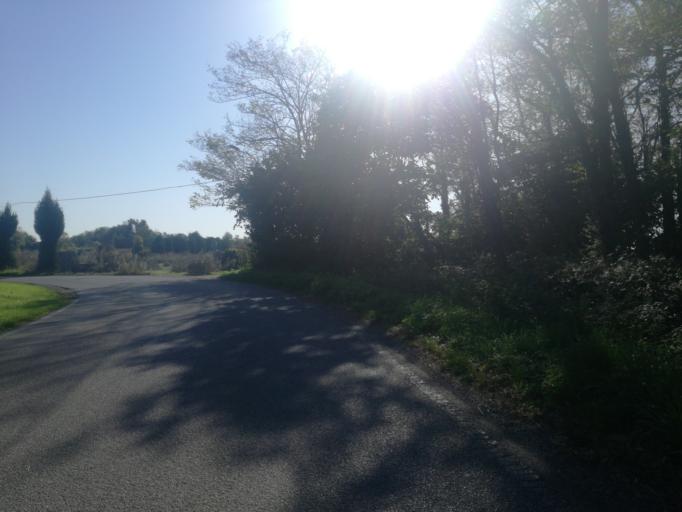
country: IT
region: Lombardy
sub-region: Provincia di Monza e Brianza
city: Porto d'Adda
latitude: 45.6460
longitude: 9.4794
